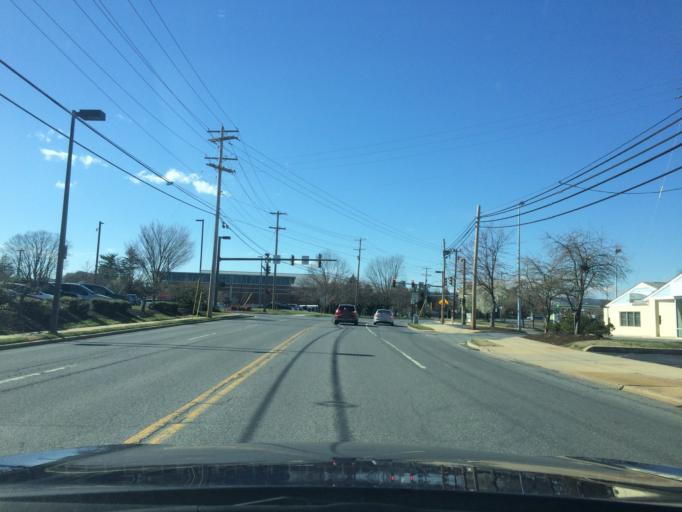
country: US
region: Maryland
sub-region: Frederick County
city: Frederick
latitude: 39.4238
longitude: -77.4141
